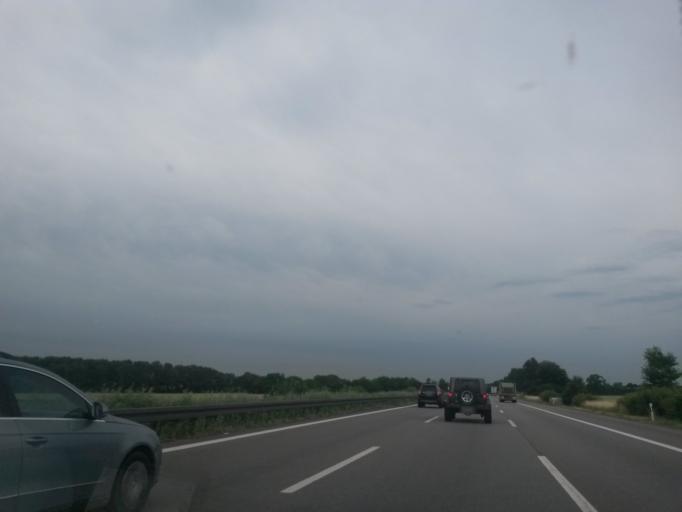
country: DE
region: Bavaria
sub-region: Upper Bavaria
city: Lenting
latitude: 48.7935
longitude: 11.4620
